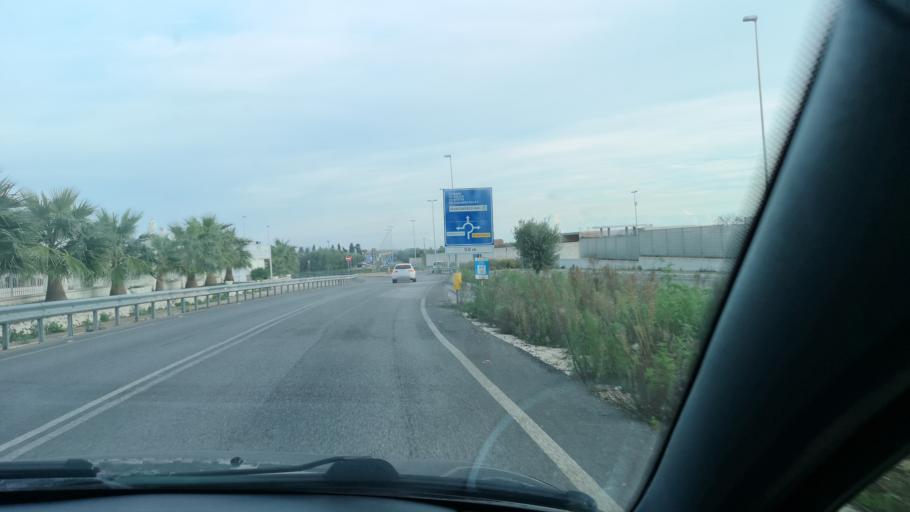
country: IT
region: Apulia
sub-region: Provincia di Bari
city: Sannicandro di Bari
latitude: 40.9847
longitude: 16.7958
